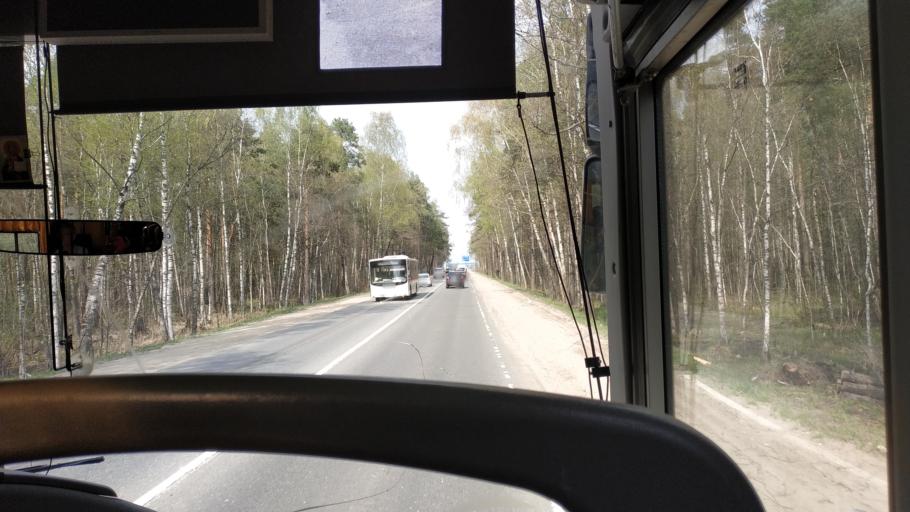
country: RU
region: Moskovskaya
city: Lytkarino
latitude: 55.6074
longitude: 37.9176
